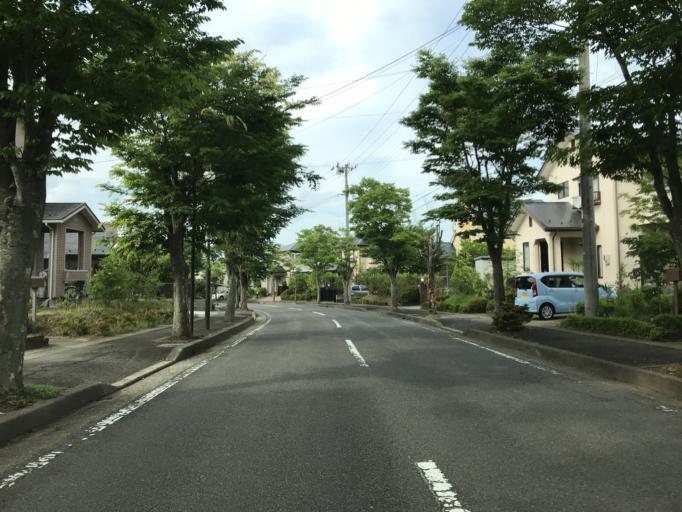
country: JP
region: Fukushima
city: Nihommatsu
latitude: 37.6619
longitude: 140.4704
